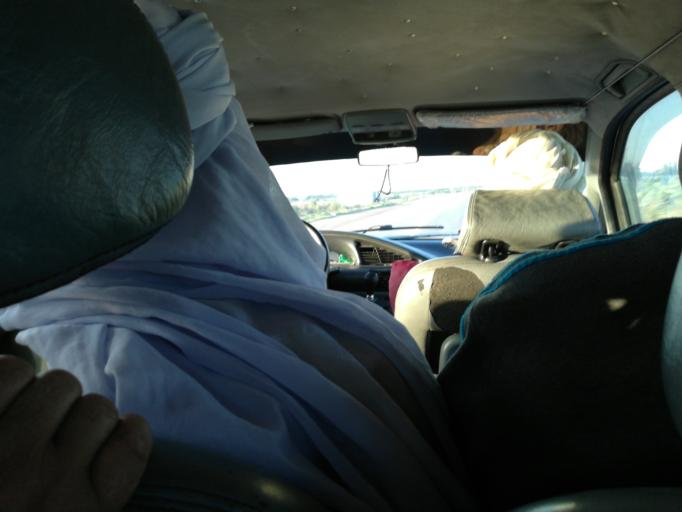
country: TN
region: Susah
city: Sidi Bou Ali
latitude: 36.0463
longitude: 10.3305
